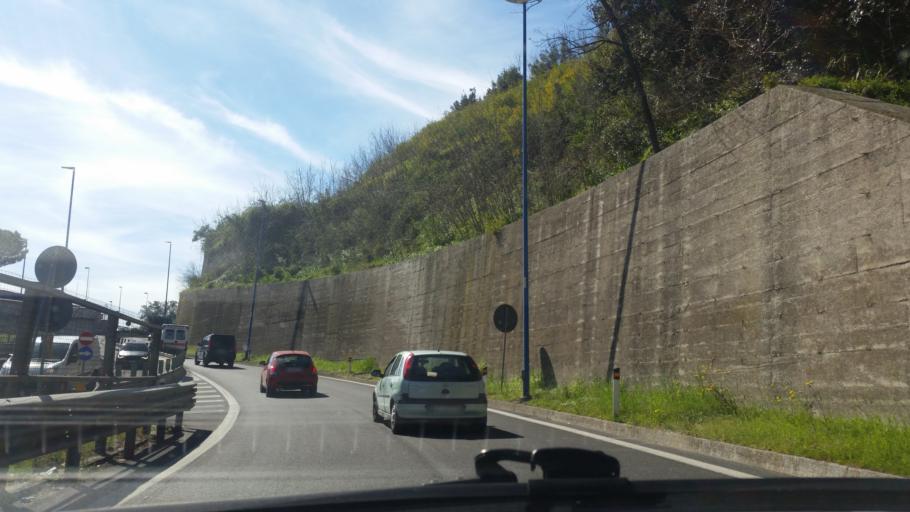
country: IT
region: Campania
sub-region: Provincia di Napoli
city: Napoli
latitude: 40.8670
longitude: 14.2424
